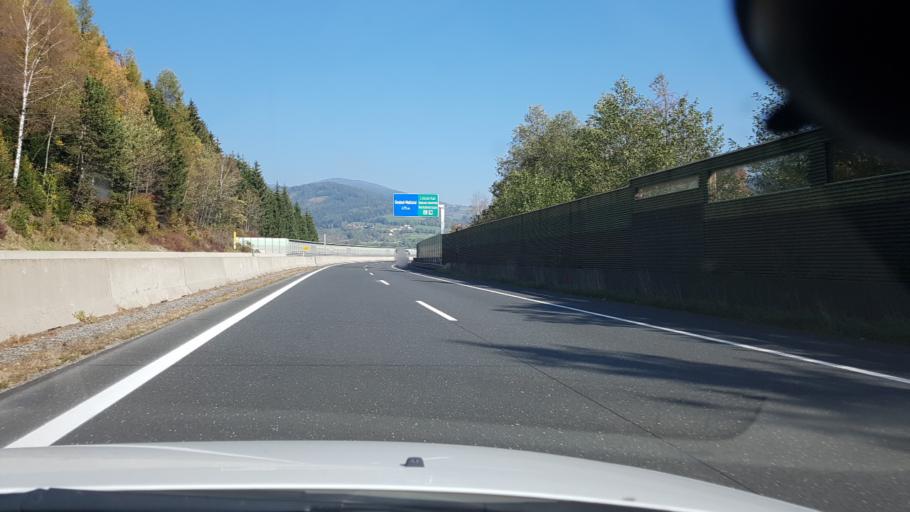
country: AT
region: Carinthia
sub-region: Politischer Bezirk Spittal an der Drau
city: Gmuend
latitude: 46.8965
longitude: 13.5261
